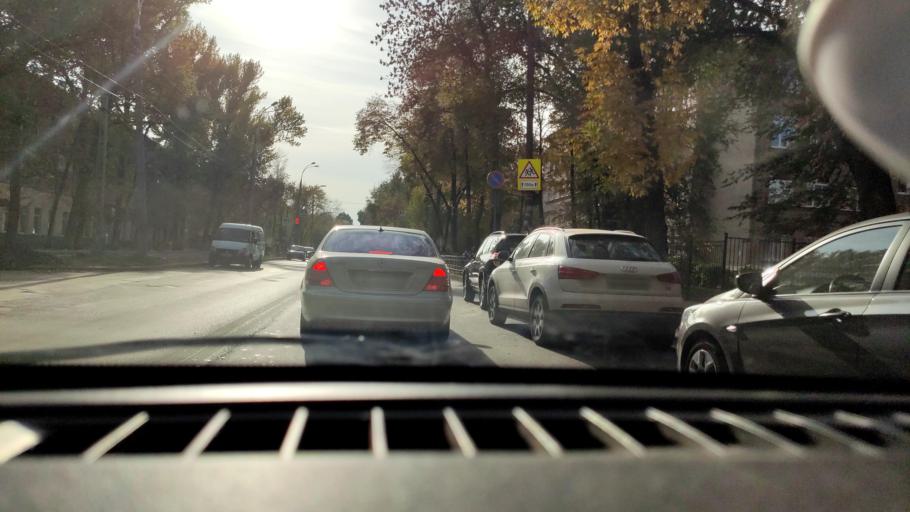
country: RU
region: Samara
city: Samara
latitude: 53.2087
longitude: 50.2442
